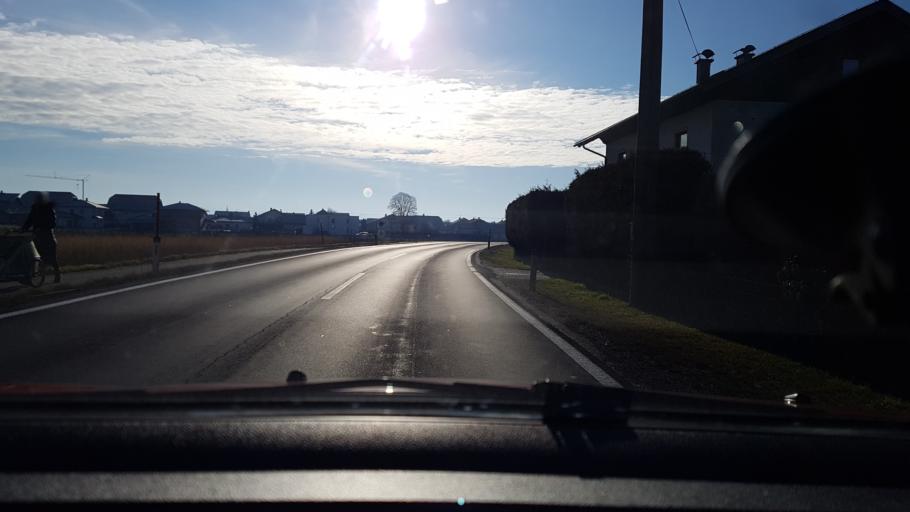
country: AT
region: Upper Austria
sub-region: Politischer Bezirk Braunau am Inn
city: Braunau am Inn
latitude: 48.1829
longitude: 13.0548
